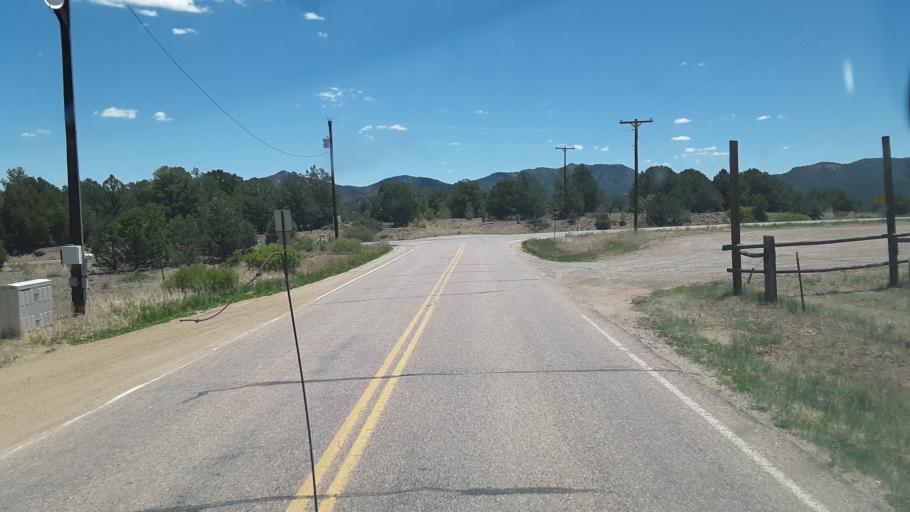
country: US
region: Colorado
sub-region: Custer County
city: Westcliffe
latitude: 38.3093
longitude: -105.6210
